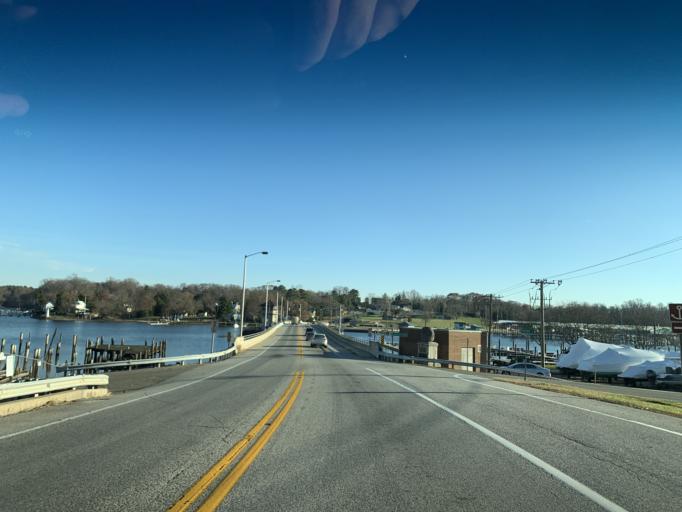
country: US
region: Delaware
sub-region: New Castle County
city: Middletown
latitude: 39.3657
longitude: -75.8834
